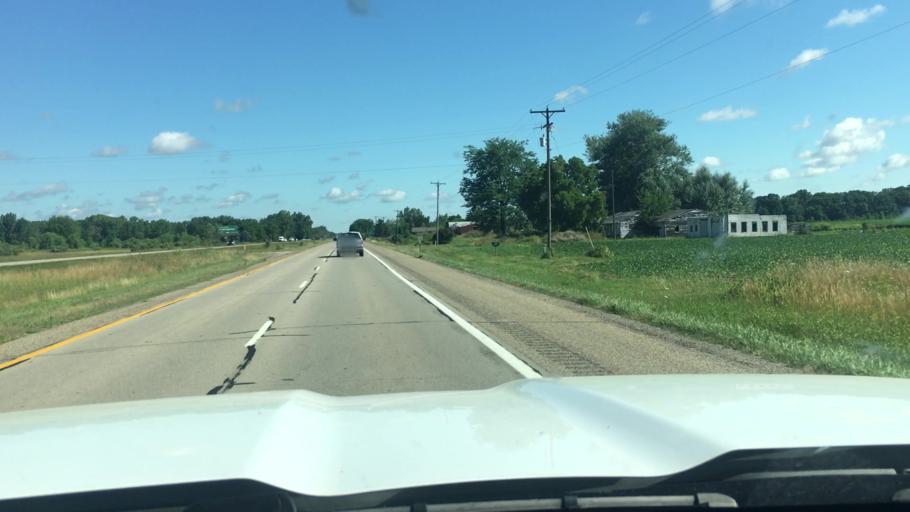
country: US
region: Michigan
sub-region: Clinton County
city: Saint Johns
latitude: 43.1308
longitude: -84.5631
